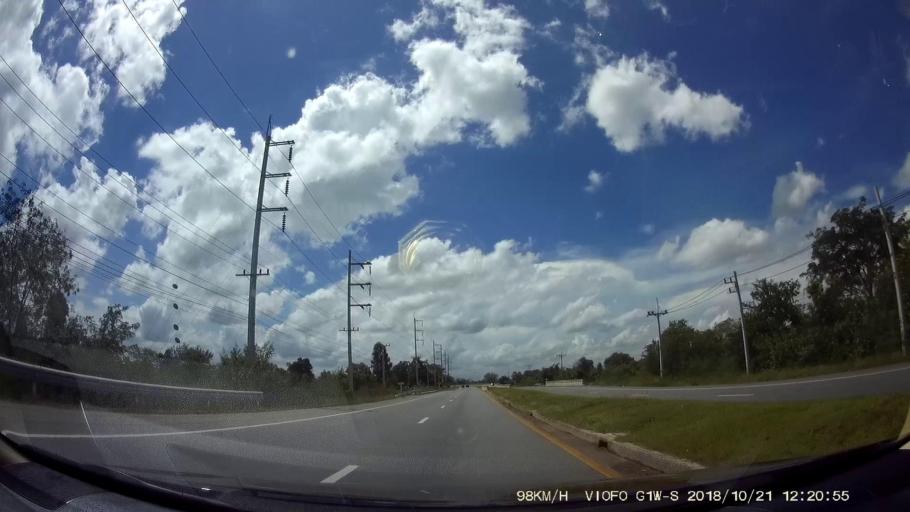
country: TH
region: Nakhon Ratchasima
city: Dan Khun Thot
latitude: 15.2818
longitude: 101.7977
